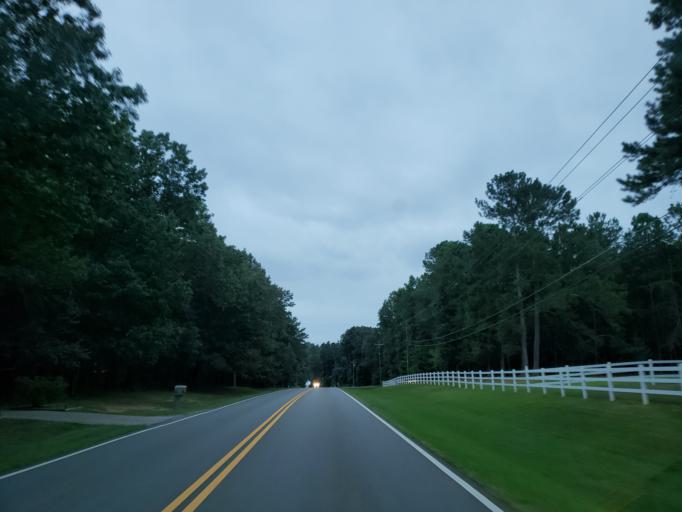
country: US
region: Georgia
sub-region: Cherokee County
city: Canton
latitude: 34.3234
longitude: -84.4686
